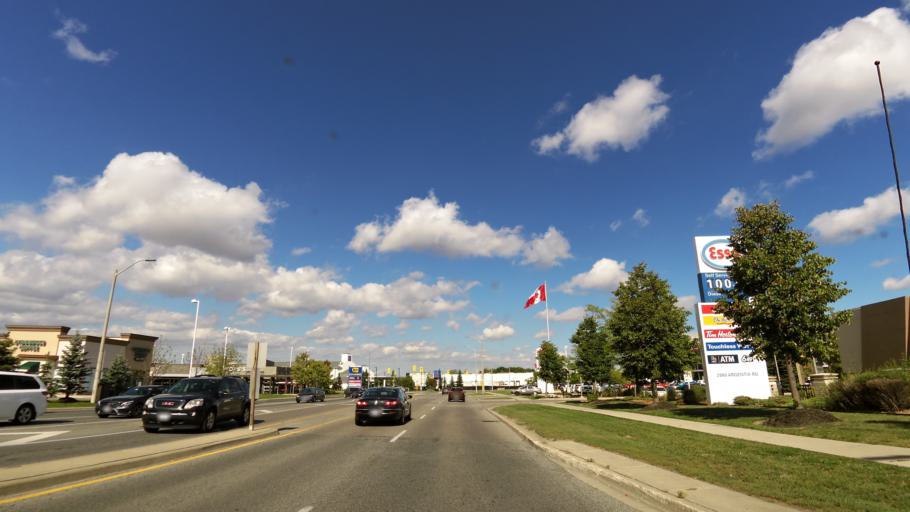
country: CA
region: Ontario
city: Brampton
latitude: 43.5975
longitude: -79.7838
